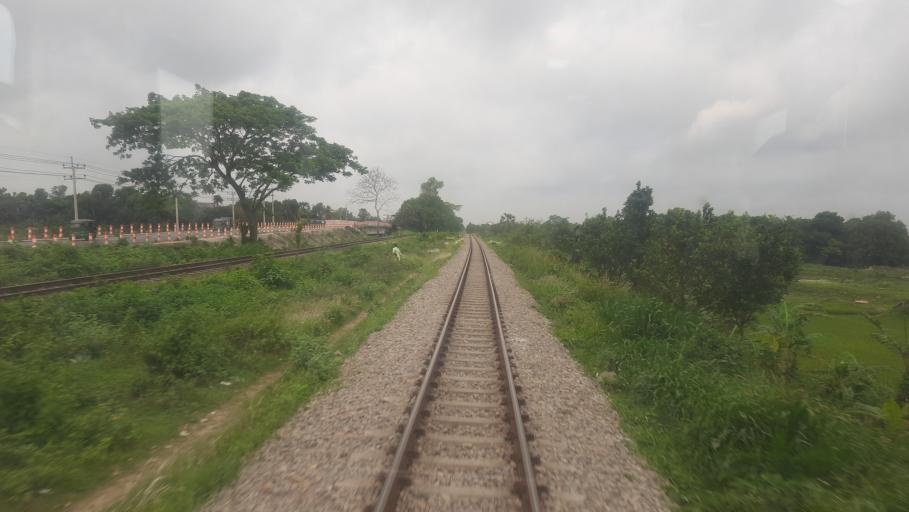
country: BD
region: Dhaka
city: Narsingdi
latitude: 23.9318
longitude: 90.7397
